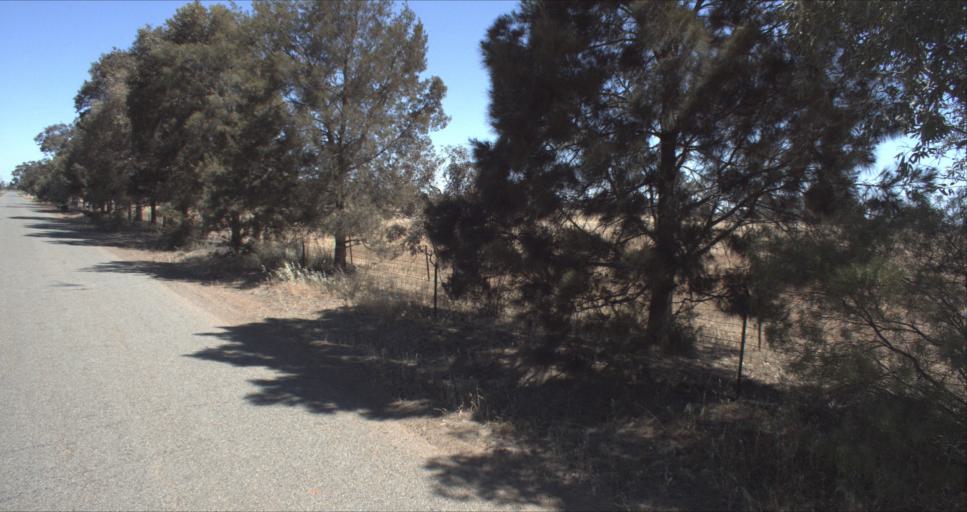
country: AU
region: New South Wales
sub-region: Leeton
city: Leeton
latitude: -34.4978
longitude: 146.4209
